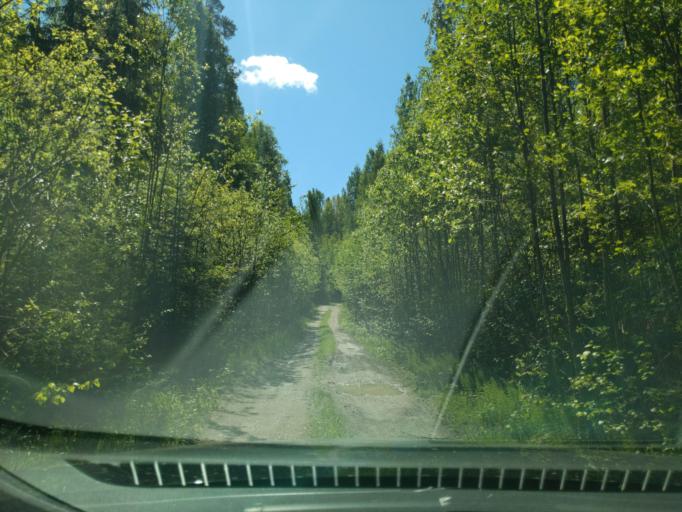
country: FI
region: Paijanne Tavastia
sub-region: Lahti
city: Lahti
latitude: 61.0477
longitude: 25.6940
